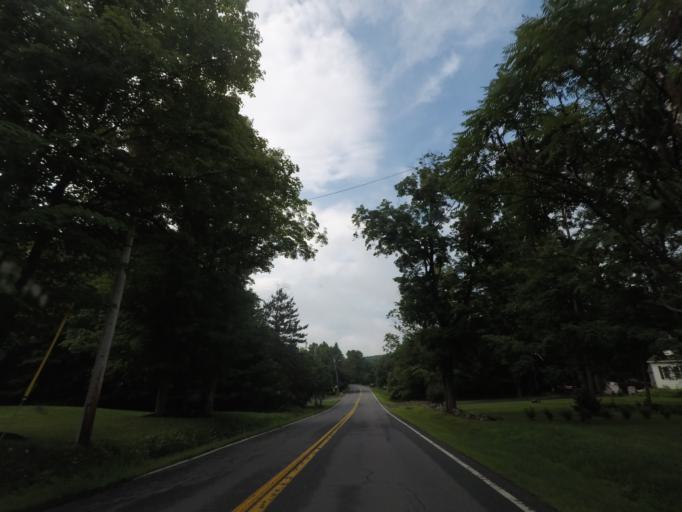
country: US
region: New York
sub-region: Rensselaer County
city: Nassau
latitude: 42.5421
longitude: -73.6088
